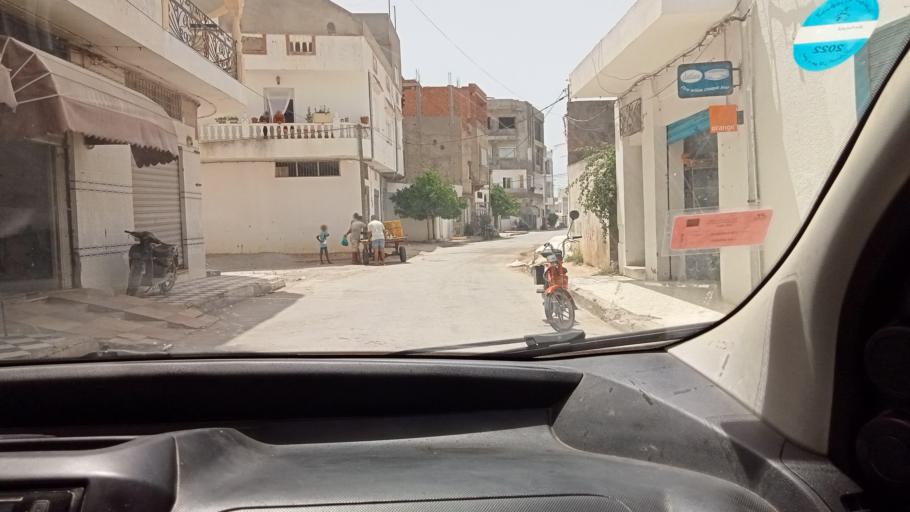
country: TN
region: Nabul
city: Qulaybiyah
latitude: 36.8550
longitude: 11.0883
